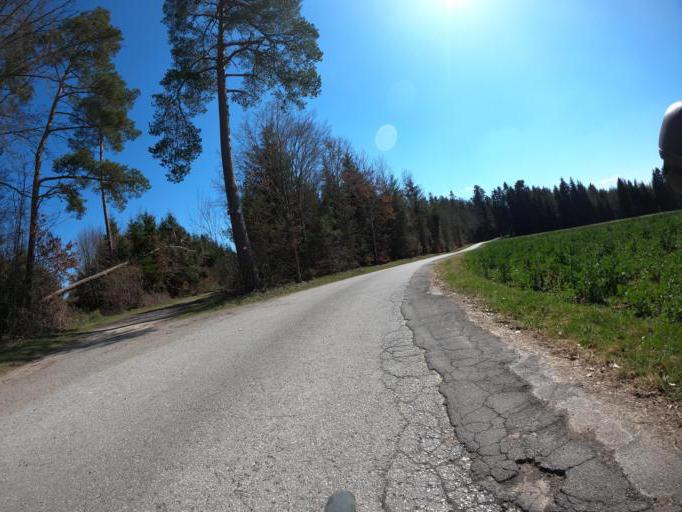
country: DE
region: Baden-Wuerttemberg
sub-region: Tuebingen Region
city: Haigerloch
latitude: 48.4215
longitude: 8.7941
